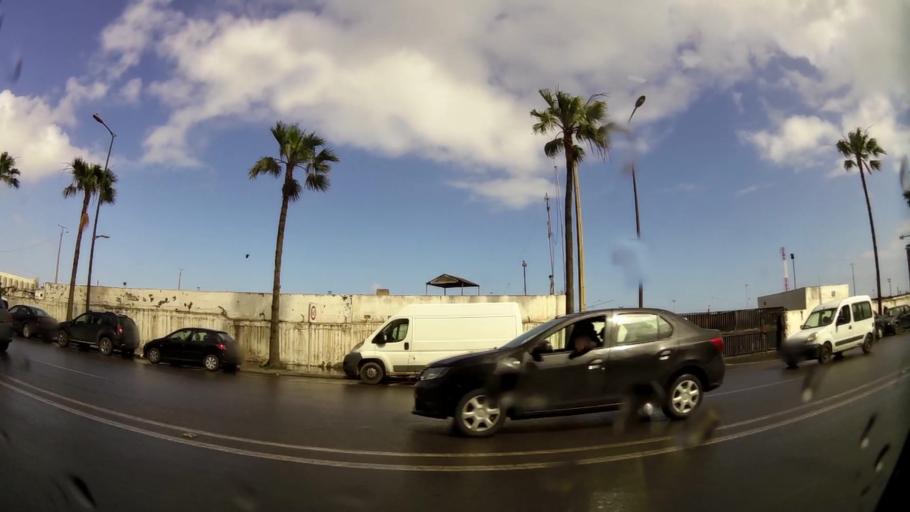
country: MA
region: Grand Casablanca
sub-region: Casablanca
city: Casablanca
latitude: 33.5996
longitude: -7.5898
